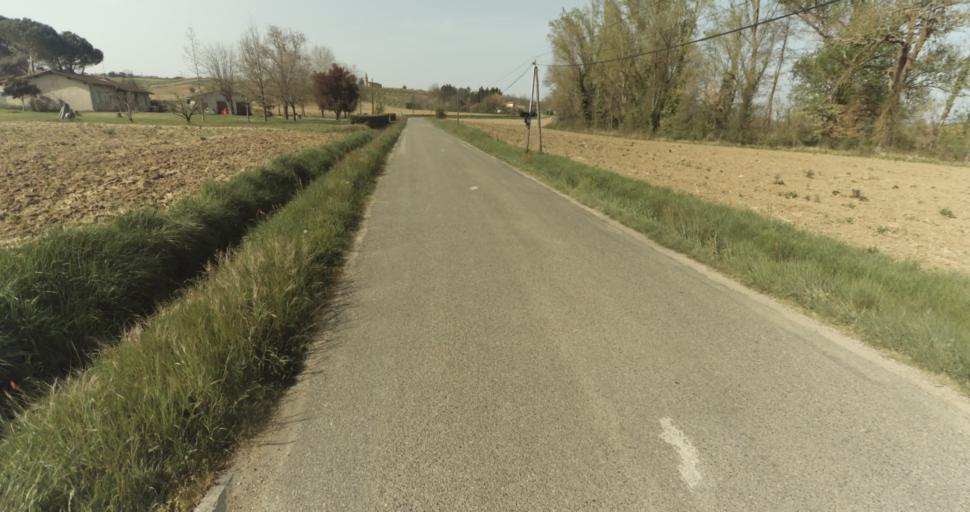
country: FR
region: Midi-Pyrenees
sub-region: Departement du Tarn-et-Garonne
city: Lafrancaise
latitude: 44.1379
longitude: 1.1754
